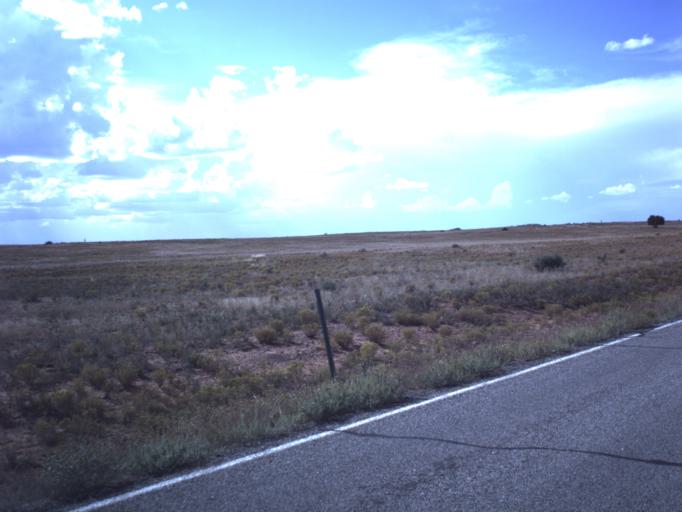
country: US
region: Utah
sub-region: Grand County
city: Moab
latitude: 38.5424
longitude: -109.7595
